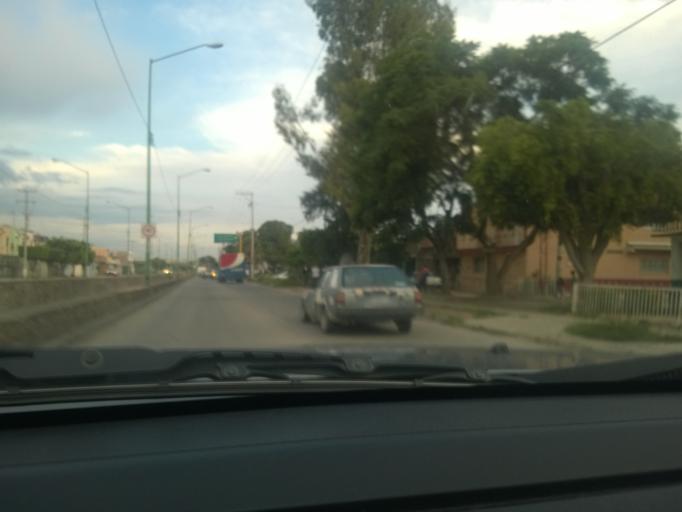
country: MX
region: Guanajuato
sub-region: Leon
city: Medina
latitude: 21.1148
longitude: -101.6292
